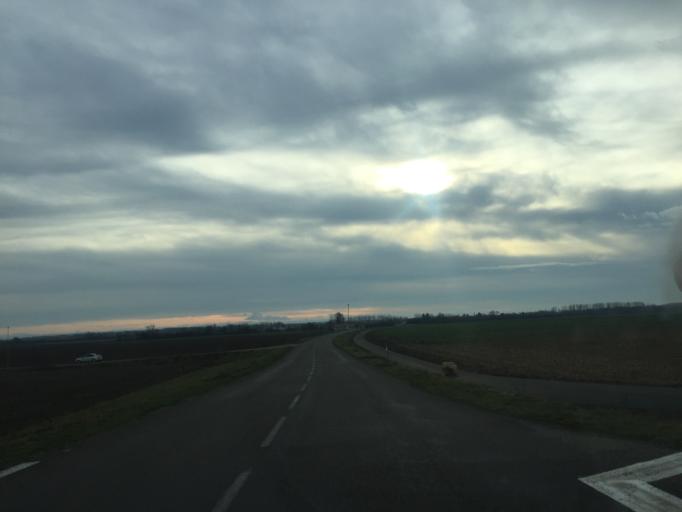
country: FR
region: Franche-Comte
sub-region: Departement du Jura
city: Tavaux
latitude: 47.0307
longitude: 5.4079
